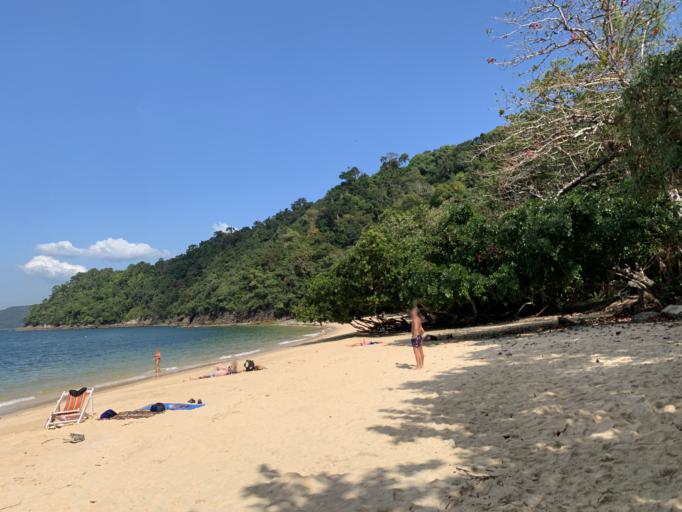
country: TH
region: Ranong
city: Kapoe
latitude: 9.7704
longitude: 98.4110
